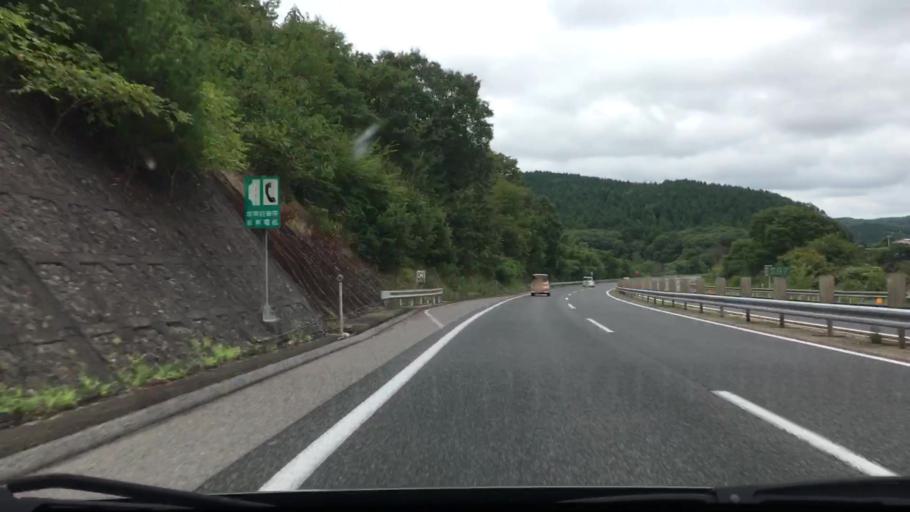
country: JP
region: Hiroshima
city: Miyoshi
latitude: 34.7749
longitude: 132.8366
